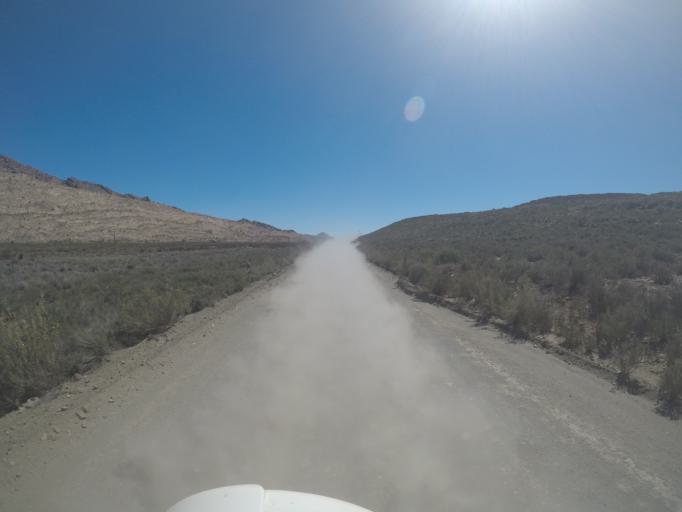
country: ZA
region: Western Cape
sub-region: Cape Winelands District Municipality
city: Ceres
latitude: -32.8249
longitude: 19.4541
